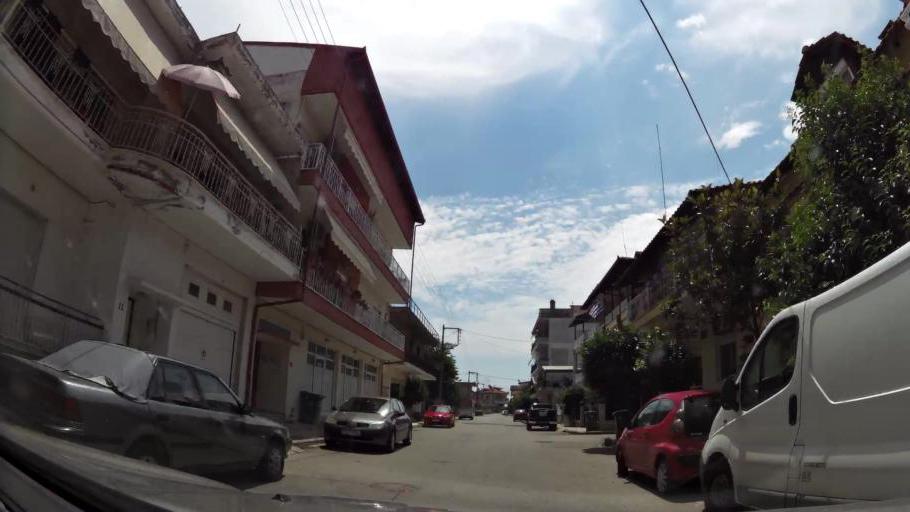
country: GR
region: Central Macedonia
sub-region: Nomos Pierias
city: Katerini
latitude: 40.2627
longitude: 22.5130
